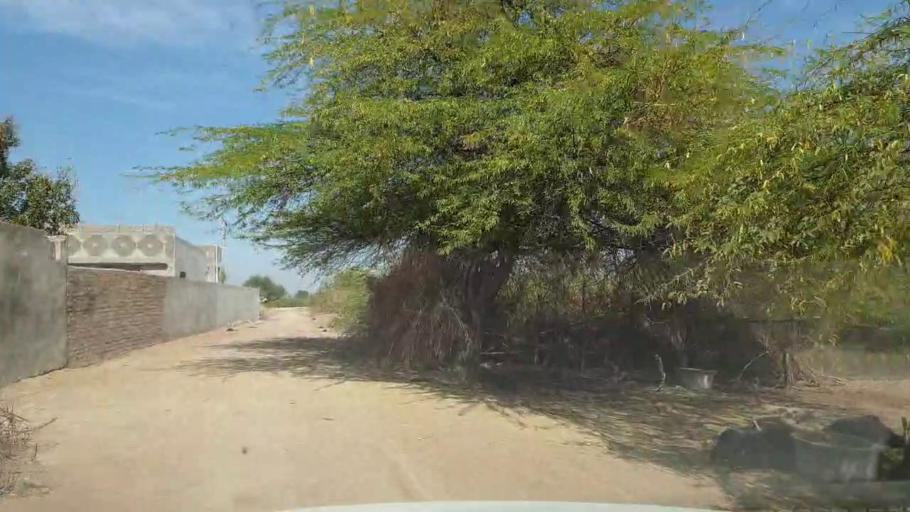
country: PK
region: Sindh
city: Mirpur Khas
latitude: 25.6254
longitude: 69.1960
